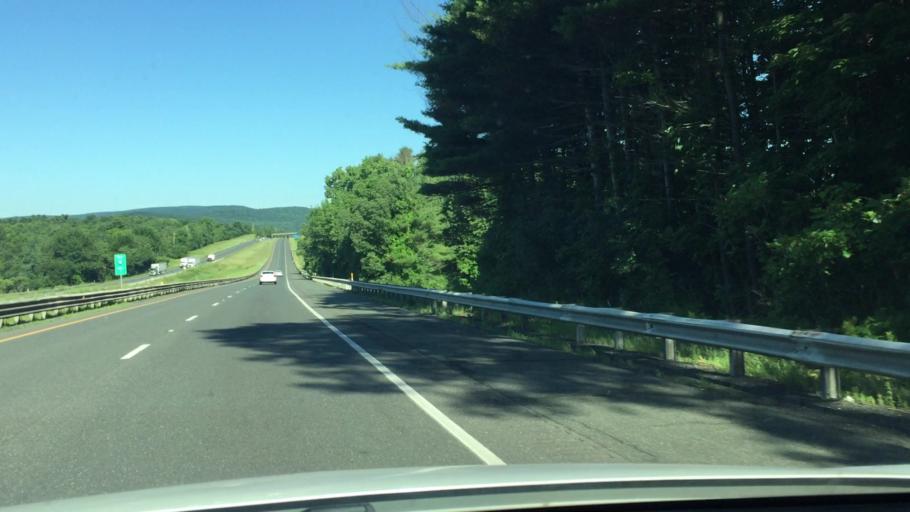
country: US
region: Massachusetts
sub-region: Berkshire County
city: Stockbridge
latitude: 42.2984
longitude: -73.3038
